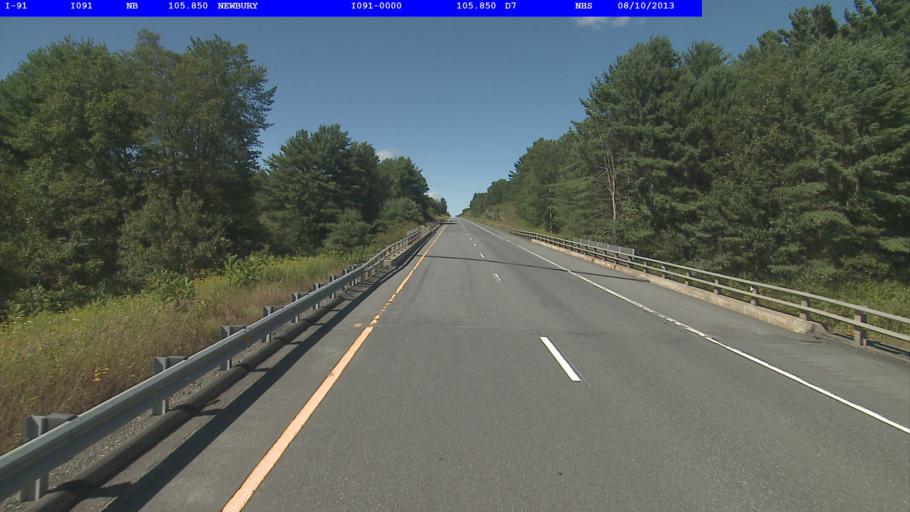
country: US
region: New Hampshire
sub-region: Grafton County
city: Haverhill
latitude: 44.0975
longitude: -72.1099
